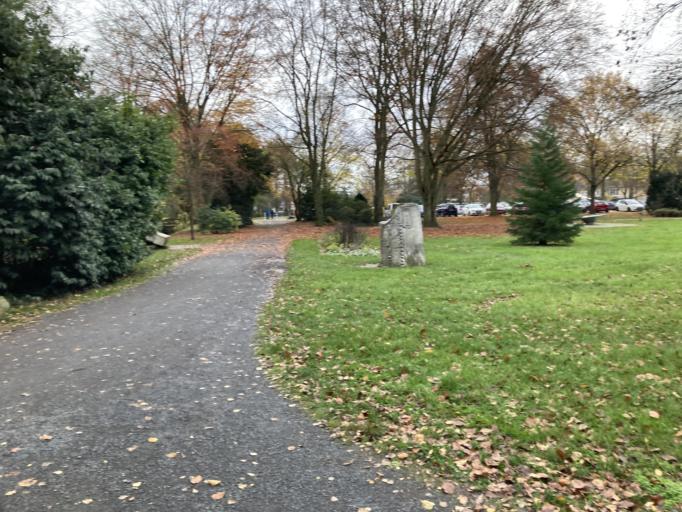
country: DE
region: North Rhine-Westphalia
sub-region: Regierungsbezirk Koln
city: Troisdorf
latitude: 50.8177
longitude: 7.1642
